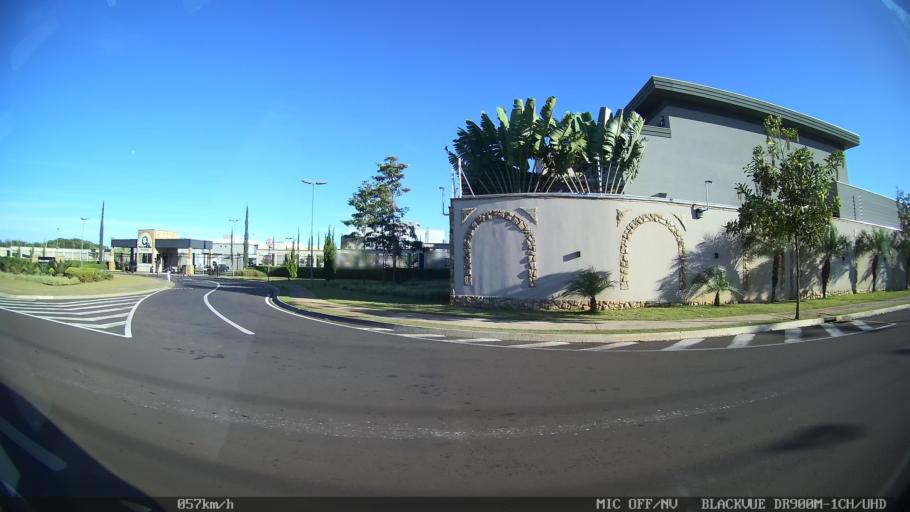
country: BR
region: Sao Paulo
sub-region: Franca
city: Franca
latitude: -20.5733
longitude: -47.4083
